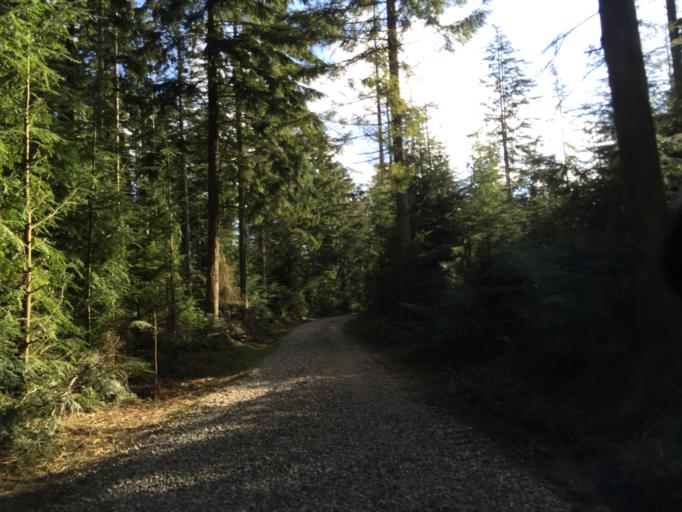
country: DK
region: Central Jutland
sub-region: Holstebro Kommune
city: Ulfborg
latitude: 56.2513
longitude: 8.4491
